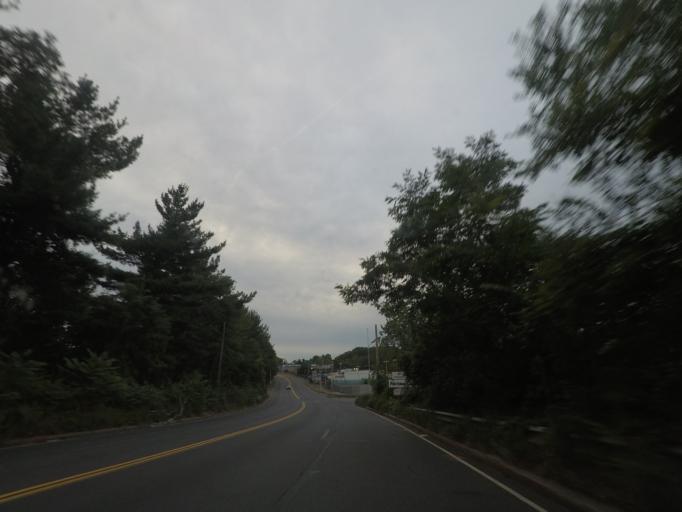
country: US
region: Massachusetts
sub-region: Hampden County
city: Ludlow
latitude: 42.1498
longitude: -72.5252
